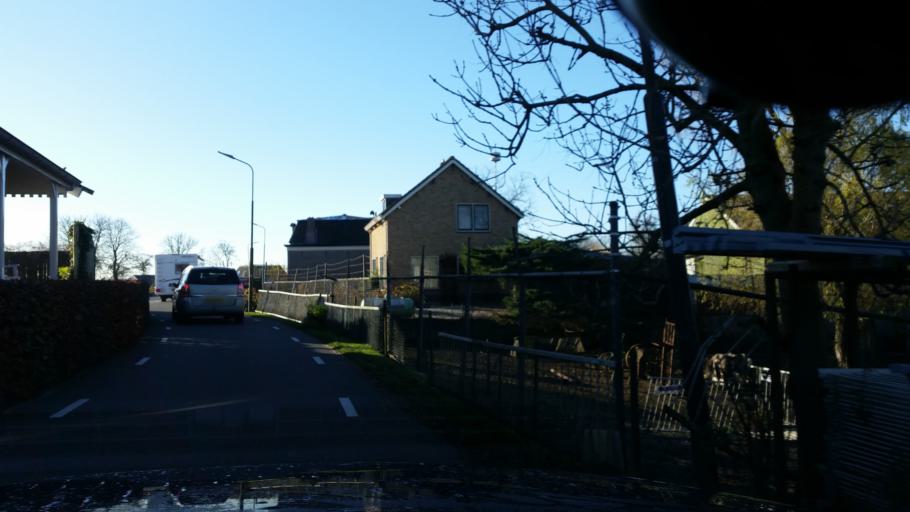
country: NL
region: North Holland
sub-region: Gemeente Ouder-Amstel
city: Ouderkerk aan de Amstel
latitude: 52.2538
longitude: 4.9119
